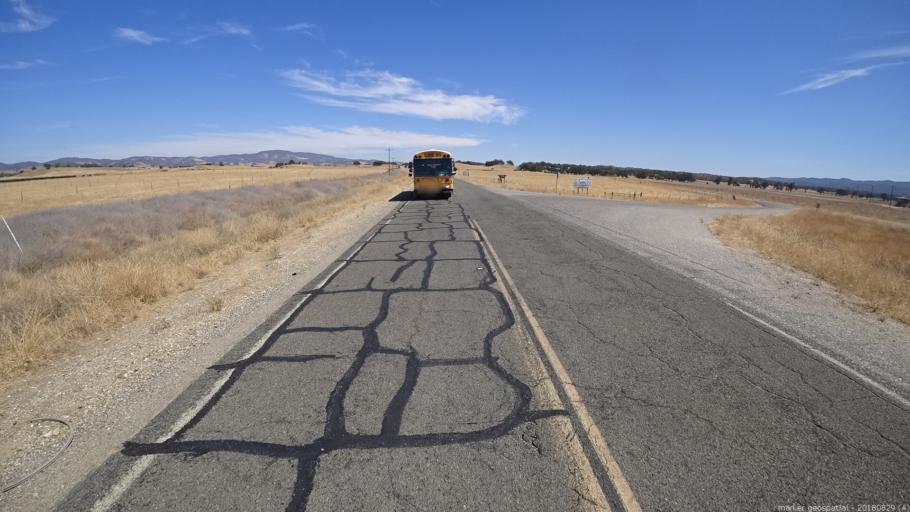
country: US
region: California
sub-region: Monterey County
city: King City
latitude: 35.9422
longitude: -121.1311
